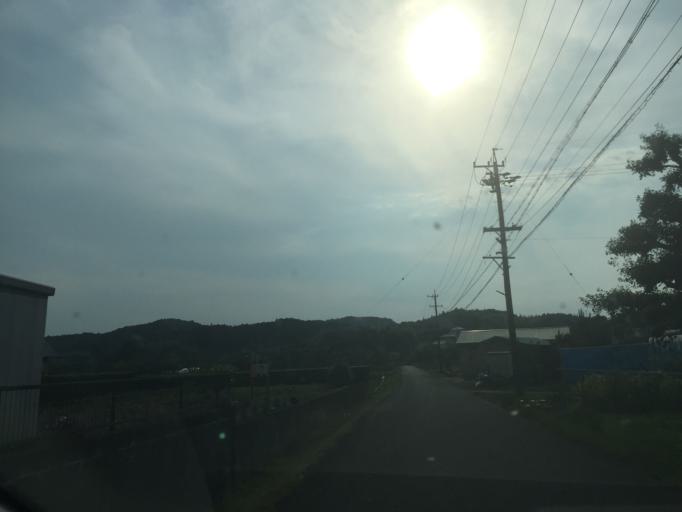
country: JP
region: Shizuoka
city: Mori
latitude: 34.8249
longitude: 137.9599
